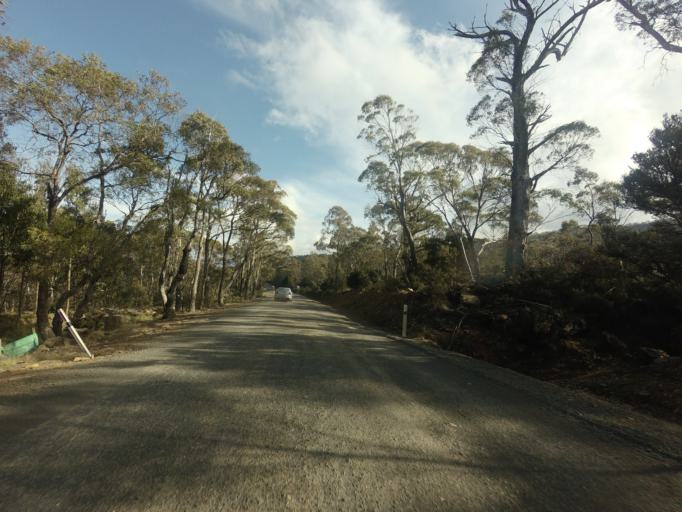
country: AU
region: Tasmania
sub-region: Meander Valley
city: Deloraine
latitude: -41.7783
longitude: 146.7098
